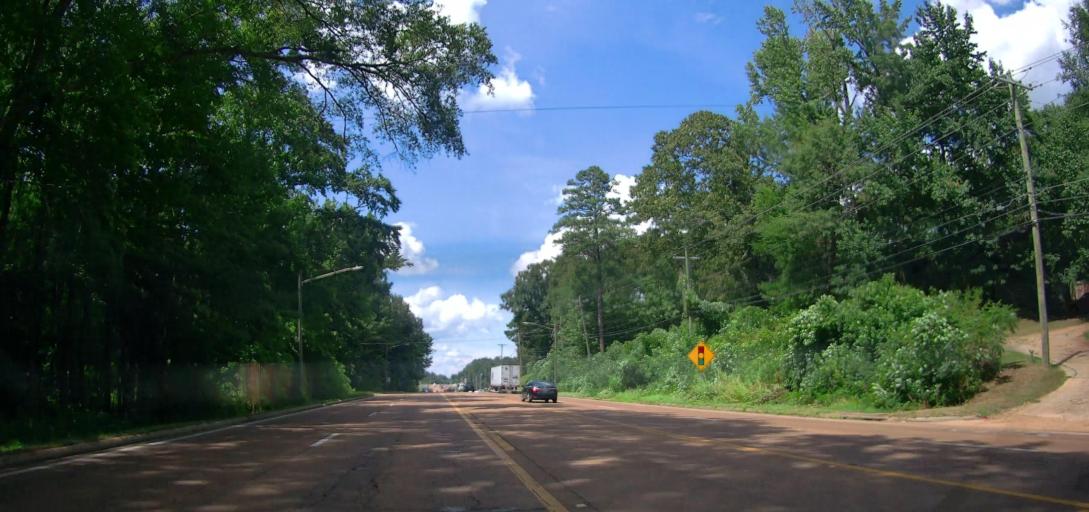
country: US
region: Mississippi
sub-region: Lowndes County
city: Columbus
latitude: 33.5544
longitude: -88.4331
